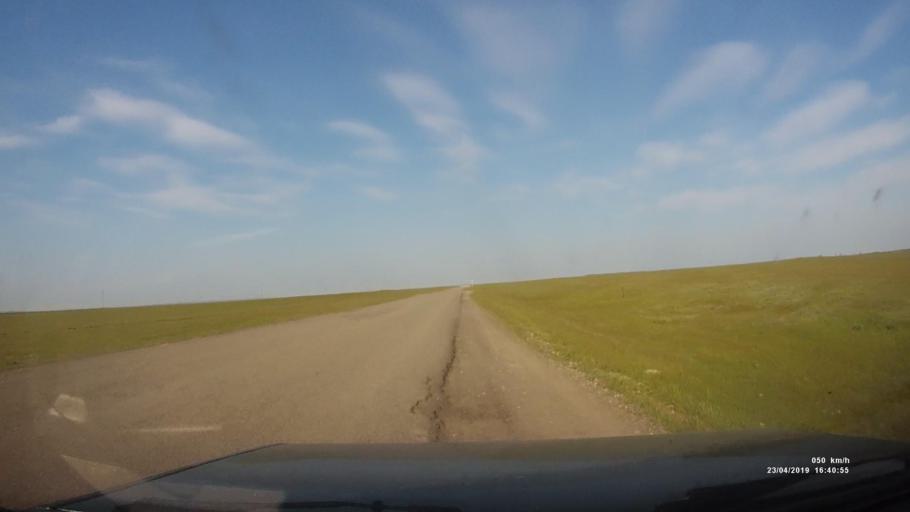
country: RU
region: Kalmykiya
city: Priyutnoye
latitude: 46.3444
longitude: 43.1816
